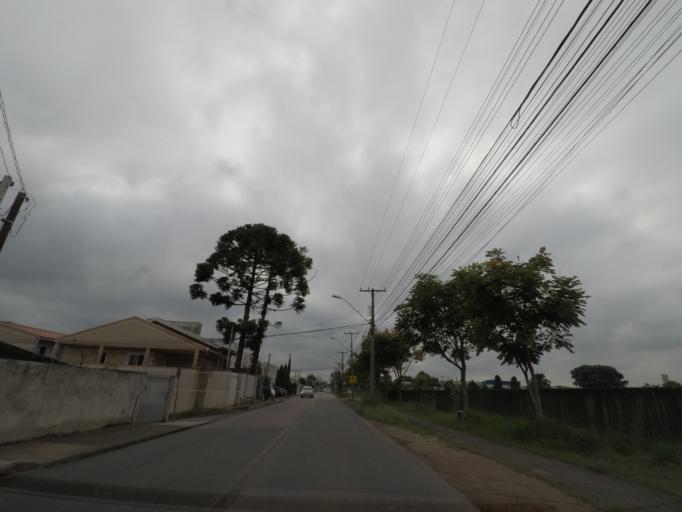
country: BR
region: Parana
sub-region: Curitiba
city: Curitiba
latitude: -25.5014
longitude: -49.3349
